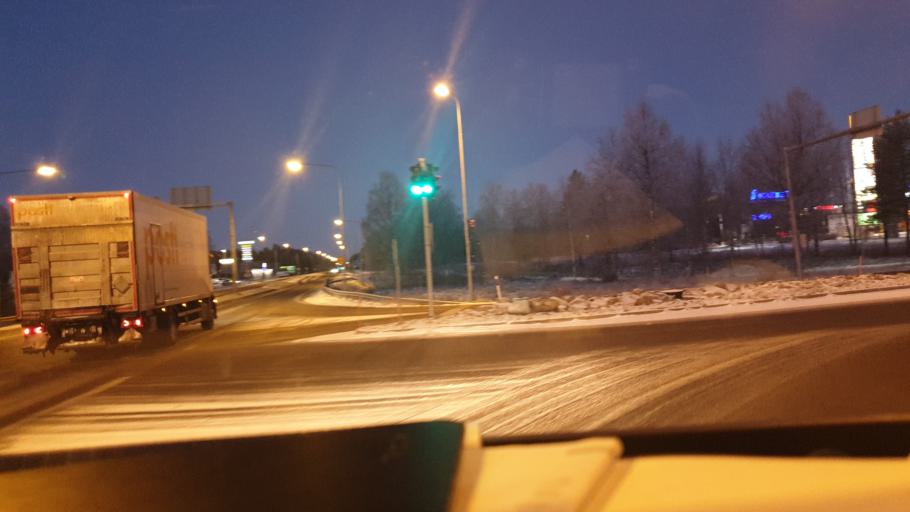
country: FI
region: Northern Ostrobothnia
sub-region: Raahe
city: Raahe
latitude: 64.6867
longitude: 24.5691
